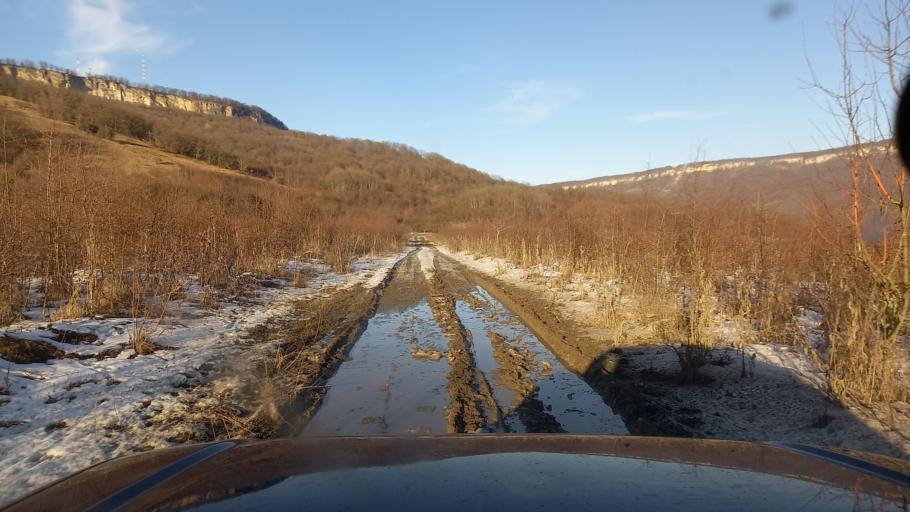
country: RU
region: Adygeya
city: Kamennomostskiy
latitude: 44.2272
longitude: 40.1708
